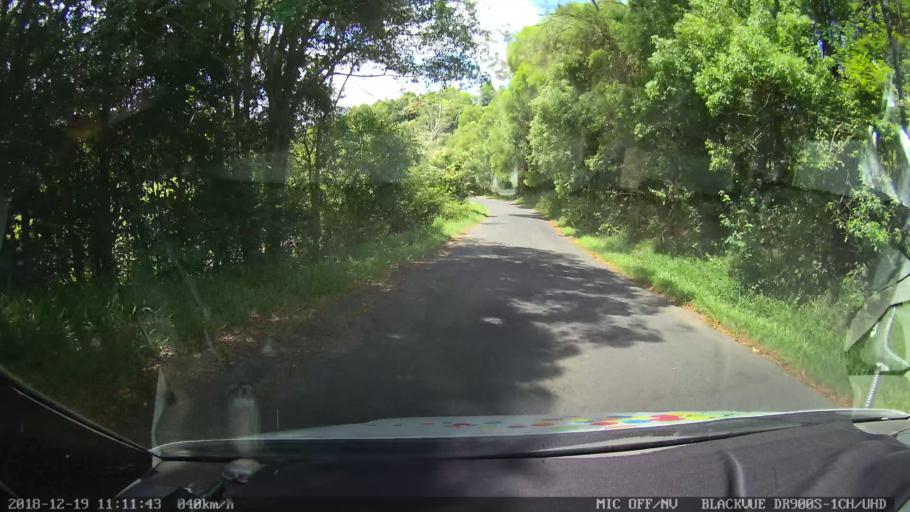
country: AU
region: New South Wales
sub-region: Lismore Municipality
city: Nimbin
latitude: -28.6449
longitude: 153.2587
